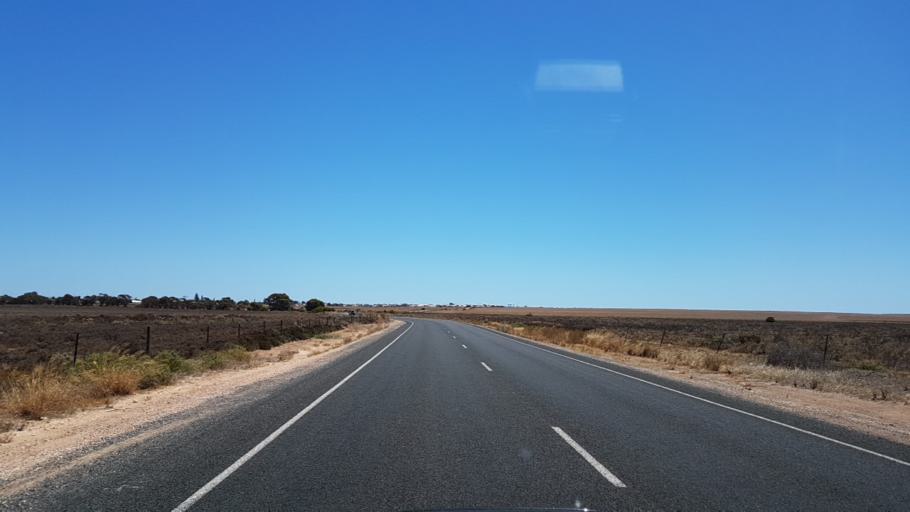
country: AU
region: South Australia
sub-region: Copper Coast
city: Wallaroo
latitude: -33.9106
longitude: 137.6427
